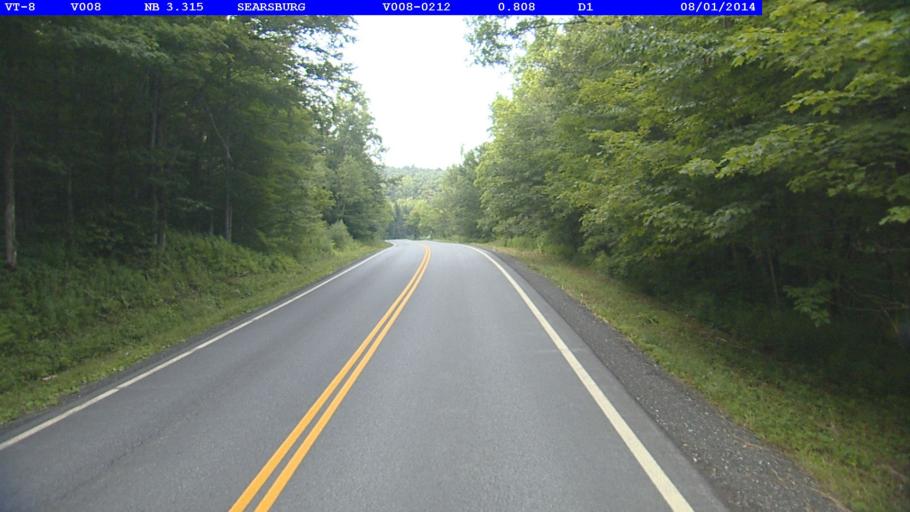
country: US
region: Vermont
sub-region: Windham County
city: Dover
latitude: 42.8688
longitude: -72.9707
